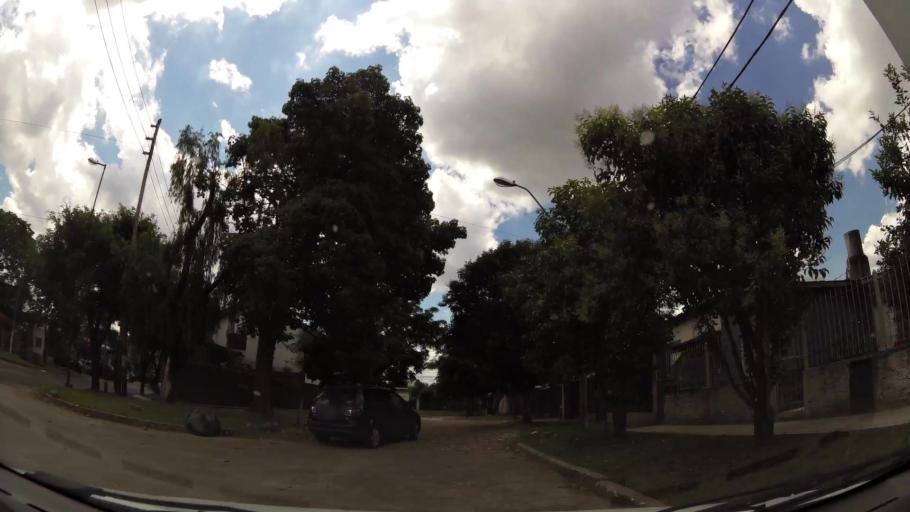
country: AR
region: Buenos Aires
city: Ituzaingo
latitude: -34.6536
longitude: -58.6797
